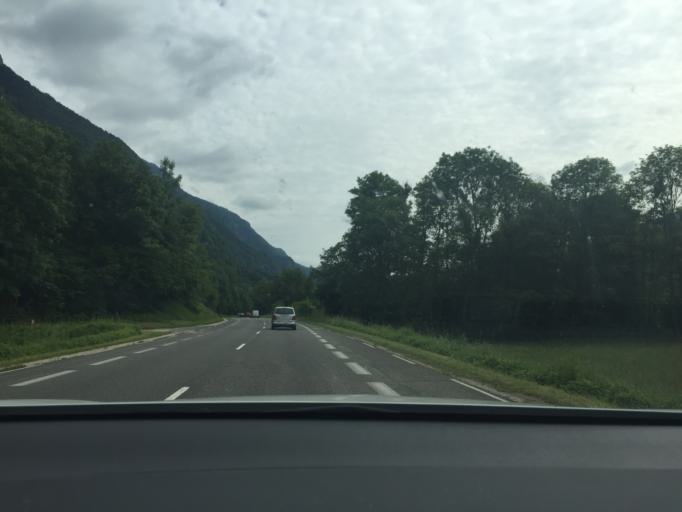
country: FR
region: Rhone-Alpes
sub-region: Departement de la Savoie
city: Vimines
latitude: 45.5117
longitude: 5.8507
